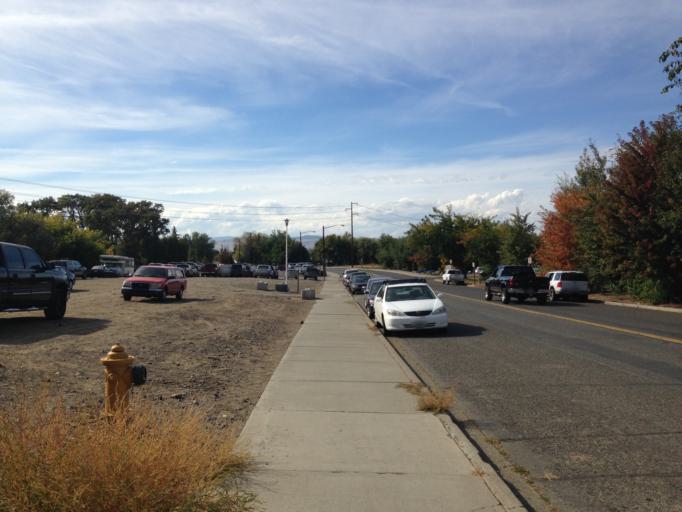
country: US
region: Washington
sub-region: Kittitas County
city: Ellensburg
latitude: 47.0060
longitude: -120.5459
